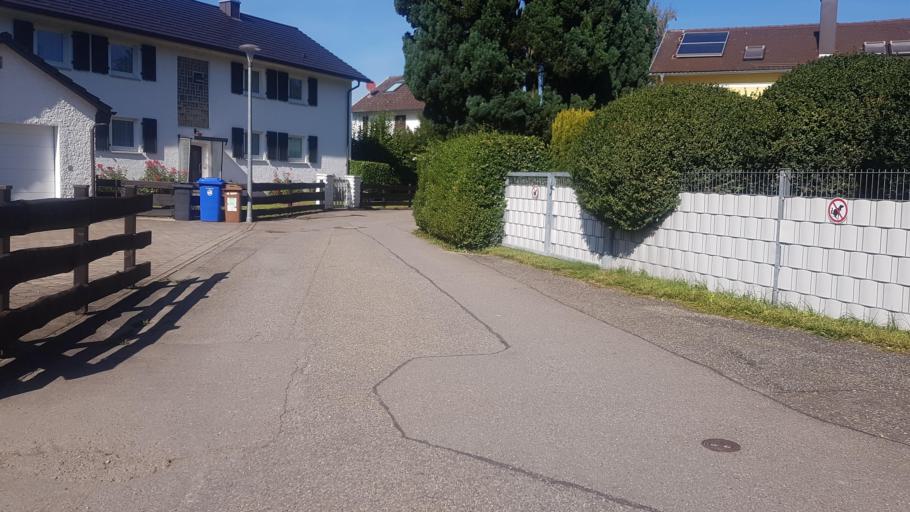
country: DE
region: Bavaria
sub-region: Swabia
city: Lindau
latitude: 47.5567
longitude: 9.6842
